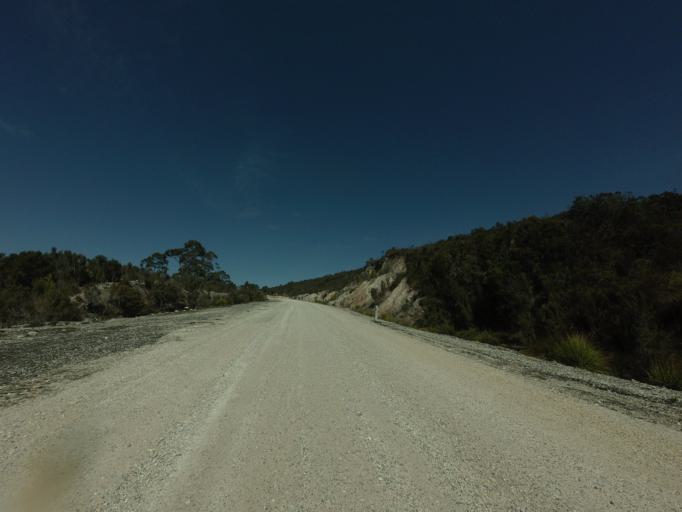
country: AU
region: Tasmania
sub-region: Huon Valley
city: Geeveston
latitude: -43.0342
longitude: 146.2922
